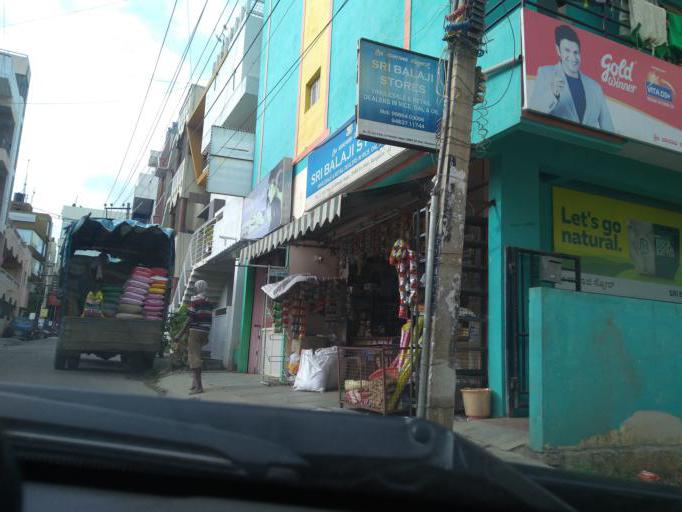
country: IN
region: Karnataka
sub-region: Bangalore Urban
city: Bangalore
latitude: 13.0082
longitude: 77.6561
